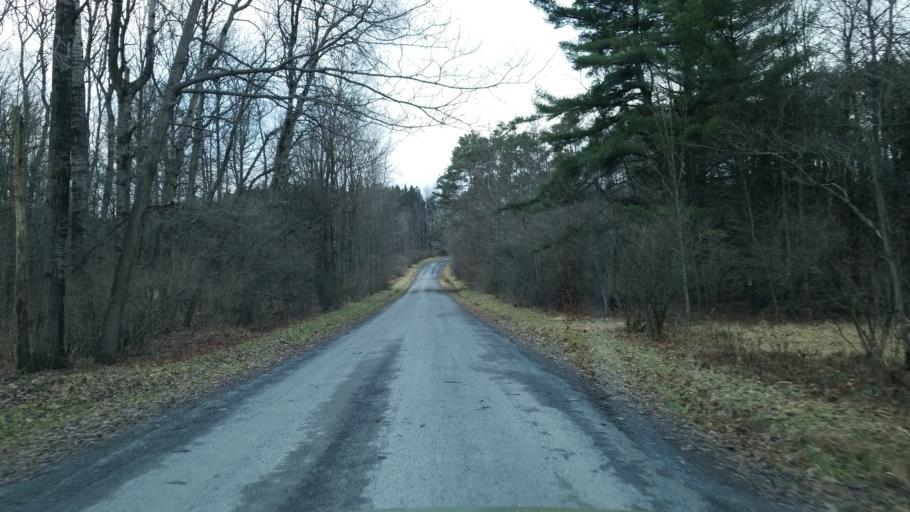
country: US
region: Pennsylvania
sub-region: Jefferson County
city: Falls Creek
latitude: 41.1824
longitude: -78.7983
